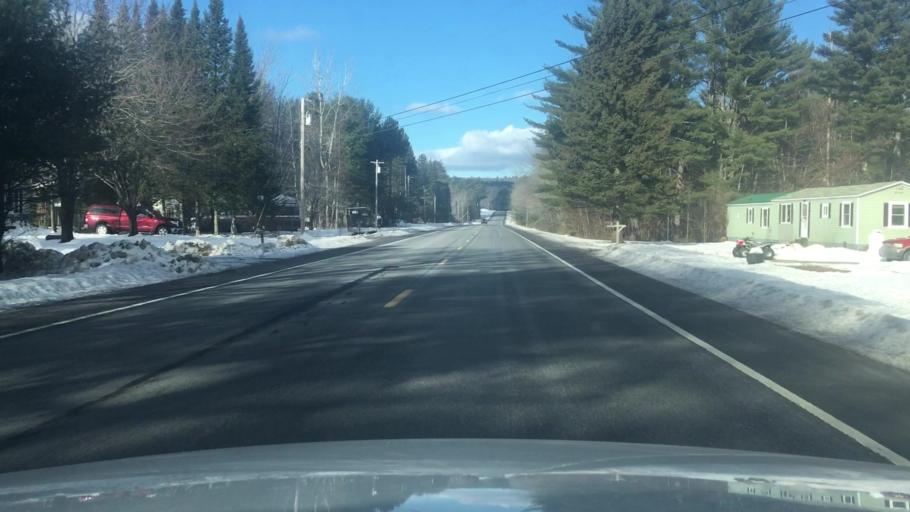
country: US
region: Maine
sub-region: Somerset County
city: Madison
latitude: 44.8524
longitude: -69.7927
